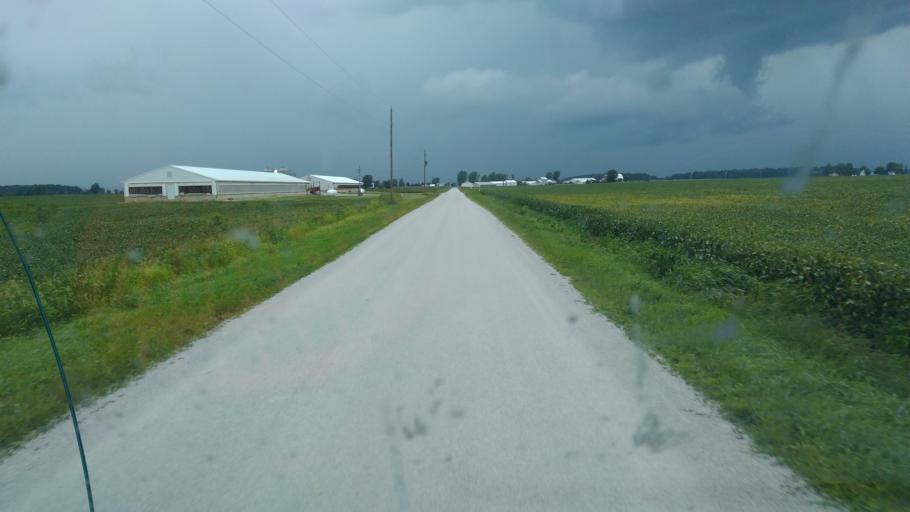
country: US
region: Ohio
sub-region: Hardin County
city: Kenton
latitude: 40.6735
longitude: -83.5145
